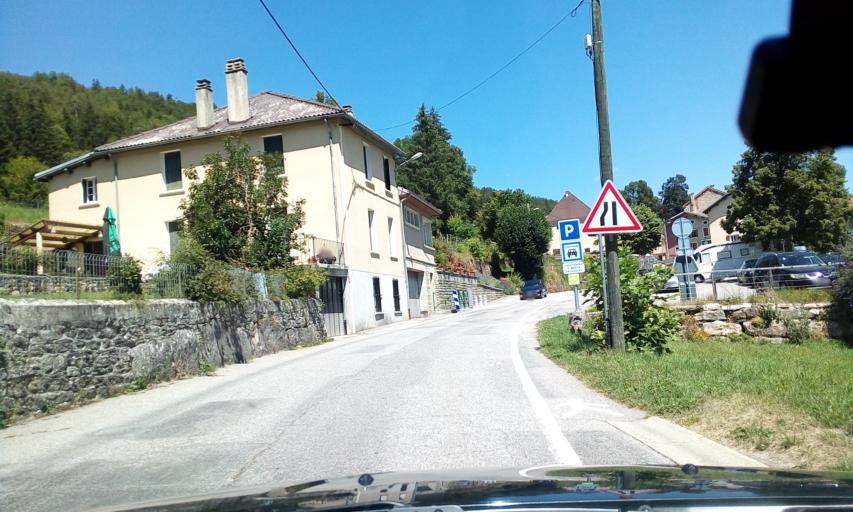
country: FR
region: Rhone-Alpes
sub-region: Departement de l'Isere
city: Pont-en-Royans
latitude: 45.0202
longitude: 5.4425
